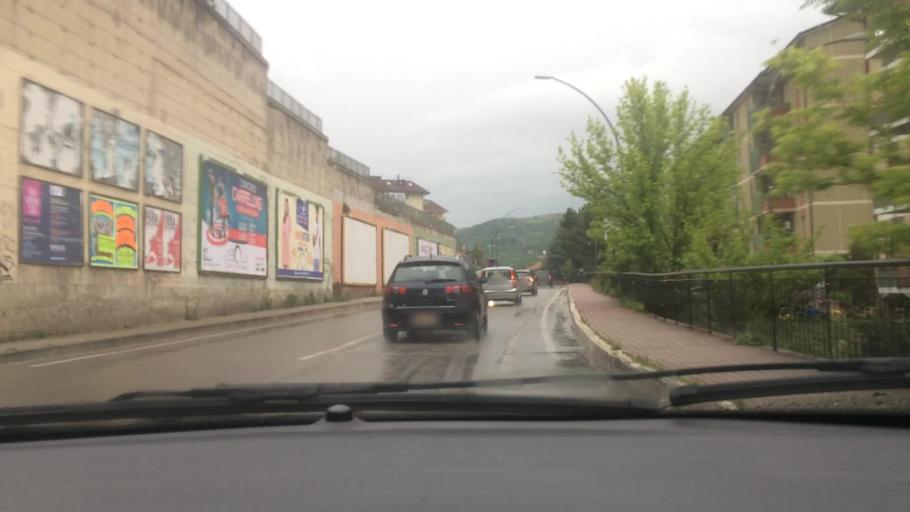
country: IT
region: Basilicate
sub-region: Provincia di Potenza
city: Potenza
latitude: 40.6437
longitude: 15.7956
